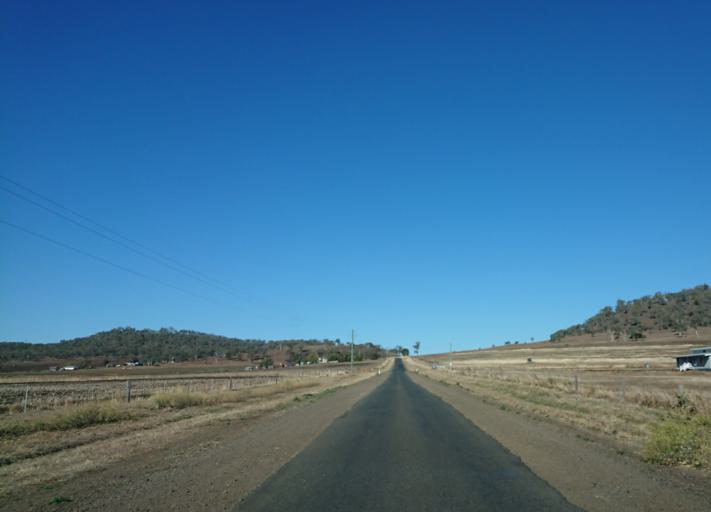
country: AU
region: Queensland
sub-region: Toowoomba
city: Top Camp
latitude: -27.8242
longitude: 152.0229
